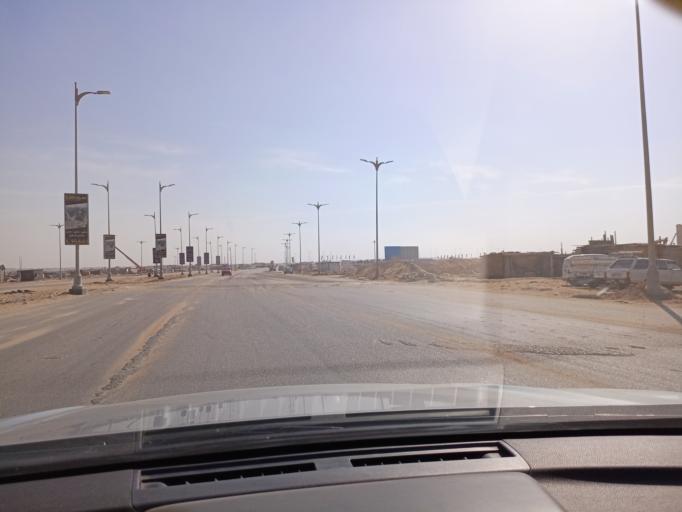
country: EG
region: Muhafazat al Qalyubiyah
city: Al Khankah
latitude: 30.0274
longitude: 31.6789
